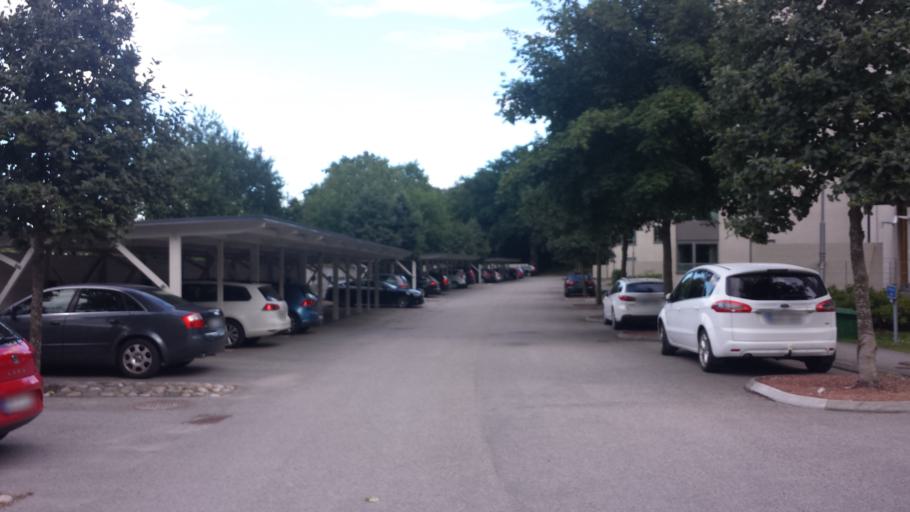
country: SE
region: Stockholm
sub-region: Solna Kommun
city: Solna
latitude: 59.3544
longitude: 18.0066
